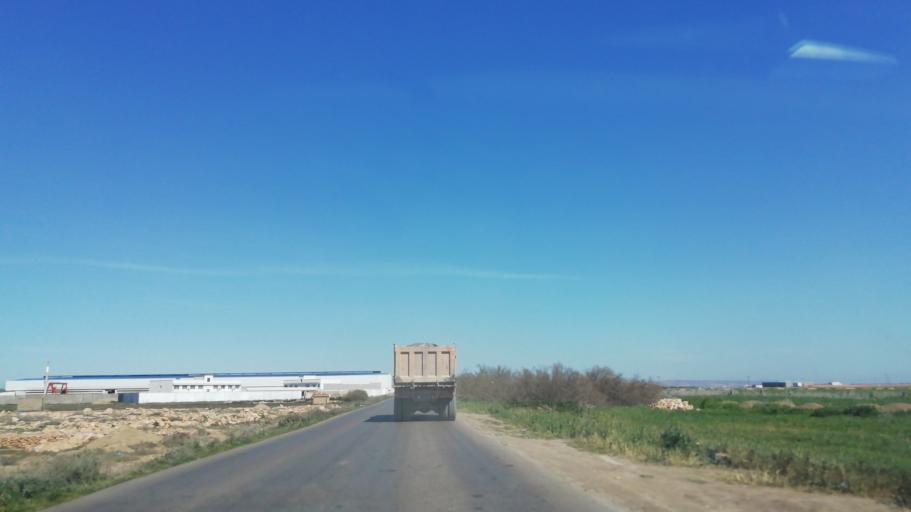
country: DZ
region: Oran
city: Es Senia
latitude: 35.5066
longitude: -0.5927
